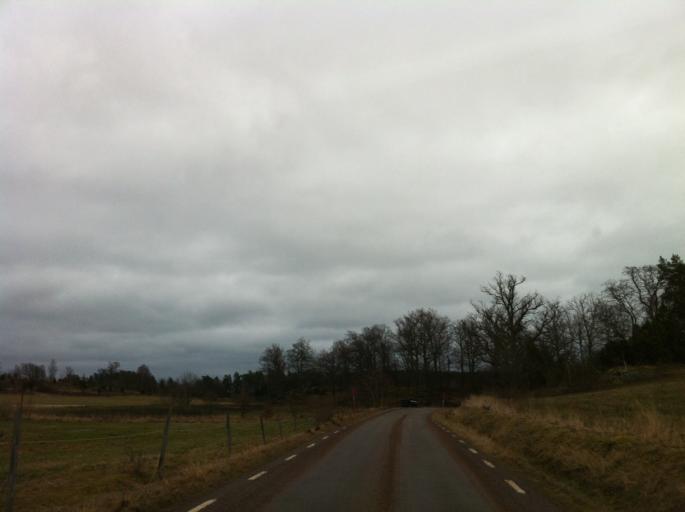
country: SE
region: Kalmar
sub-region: Vasterviks Kommun
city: Vaestervik
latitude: 57.9154
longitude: 16.6305
